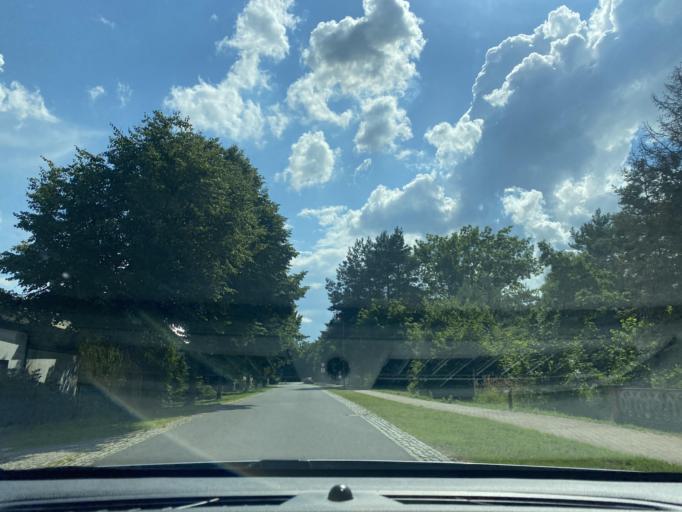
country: DE
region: Saxony
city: Boxberg
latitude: 51.4284
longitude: 14.5958
